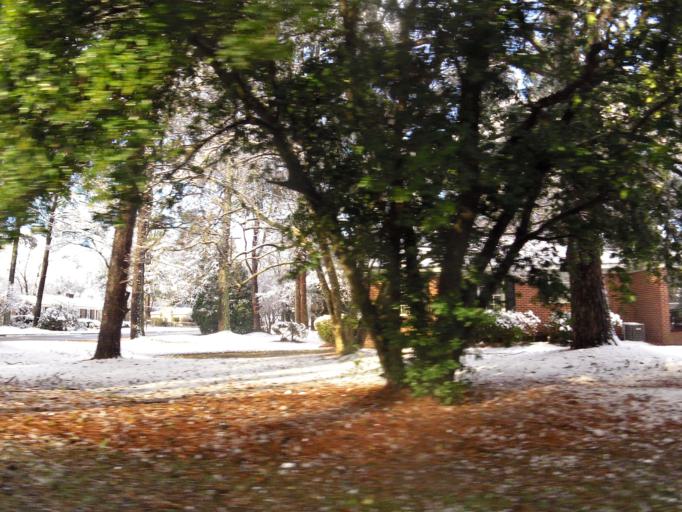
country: US
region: North Carolina
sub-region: Nash County
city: Rocky Mount
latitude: 35.9558
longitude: -77.8487
